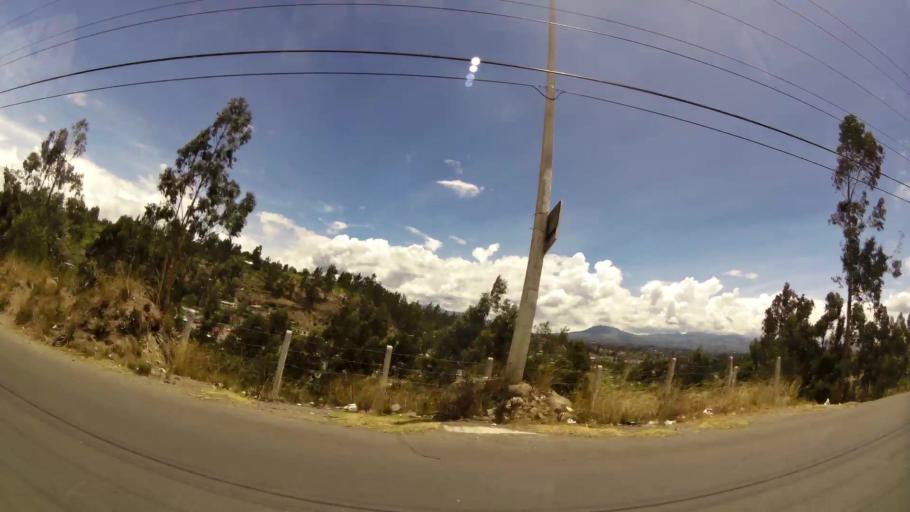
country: EC
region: Tungurahua
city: Ambato
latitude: -1.2746
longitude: -78.5892
